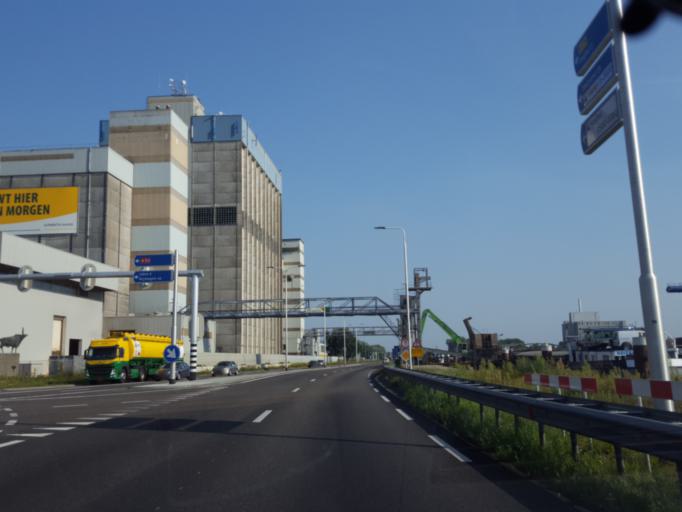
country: NL
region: North Brabant
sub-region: Gemeente Veghel
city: Eerde
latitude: 51.6233
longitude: 5.5046
